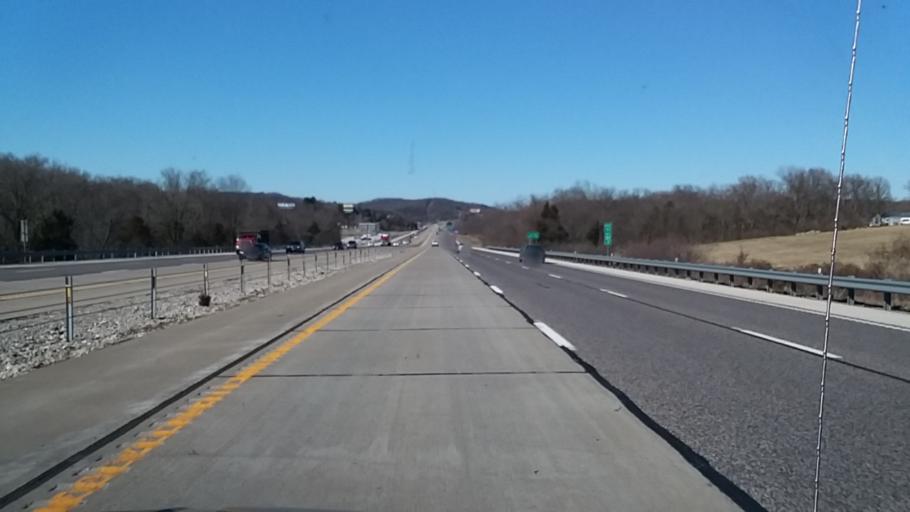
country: US
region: Missouri
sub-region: Jefferson County
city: Barnhart
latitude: 38.3319
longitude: -90.3999
